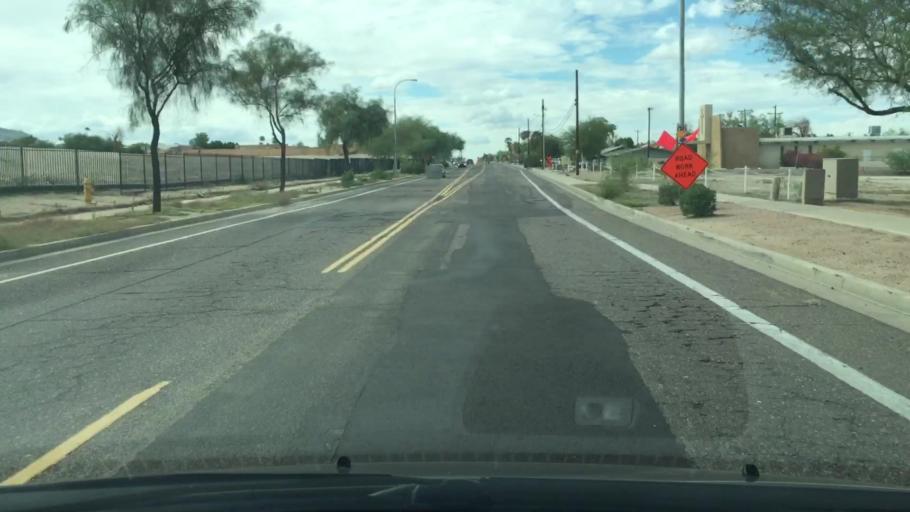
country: US
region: Arizona
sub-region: Maricopa County
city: Phoenix
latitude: 33.3633
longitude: -112.0612
